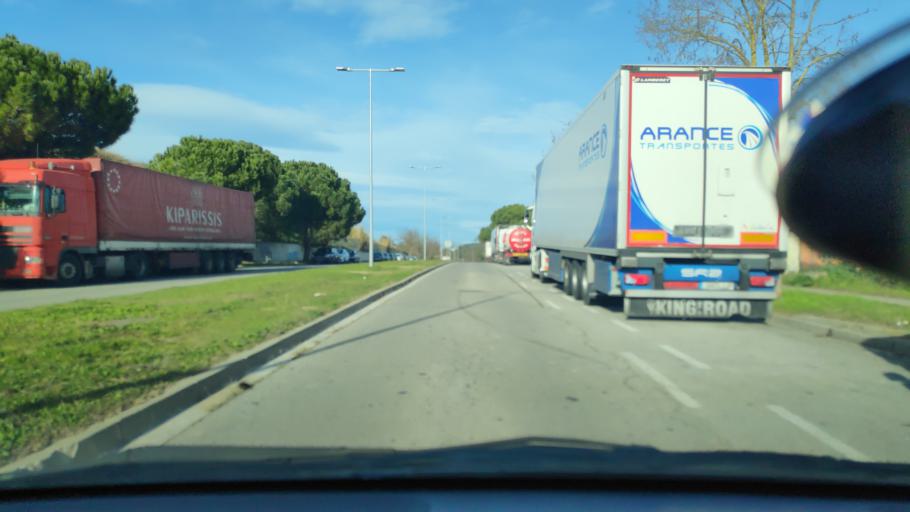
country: ES
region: Catalonia
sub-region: Provincia de Barcelona
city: Rubi
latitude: 41.4881
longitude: 2.0473
